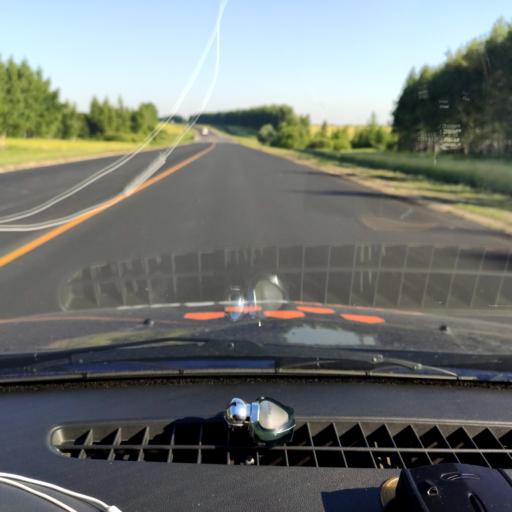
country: RU
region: Orjol
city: Zmiyevka
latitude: 52.7692
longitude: 36.3213
